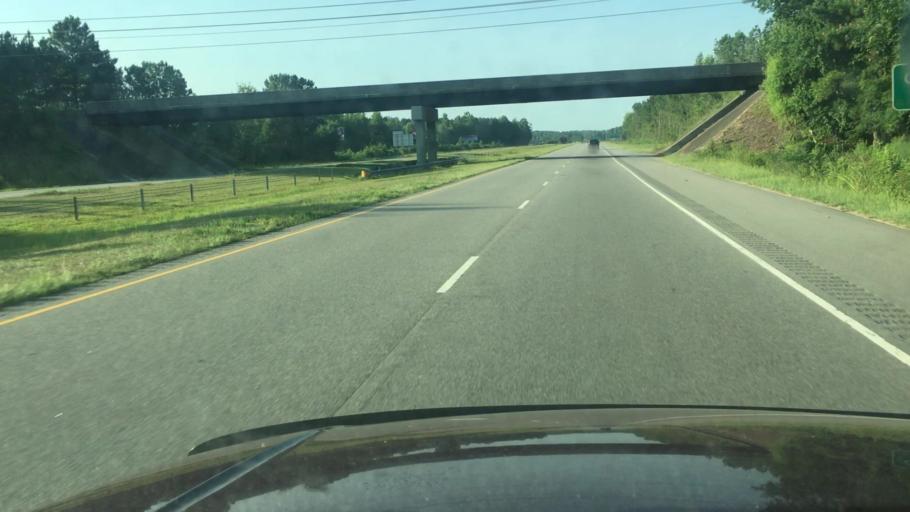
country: US
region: North Carolina
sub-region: Cumberland County
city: Fayetteville
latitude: 35.0251
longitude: -78.8725
